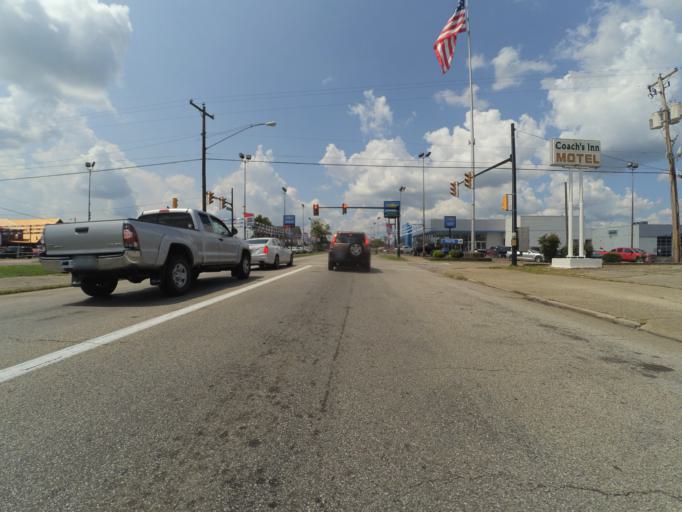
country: US
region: West Virginia
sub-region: Cabell County
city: Huntington
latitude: 38.4142
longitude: -82.4755
